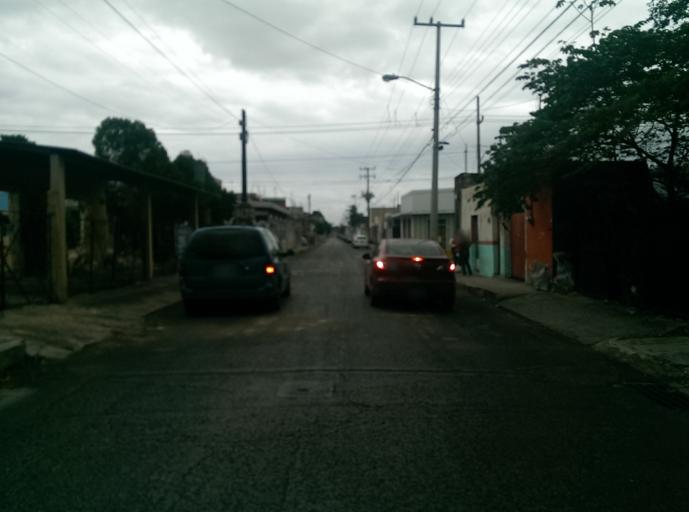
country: MX
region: Yucatan
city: Merida
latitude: 20.9773
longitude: -89.6322
